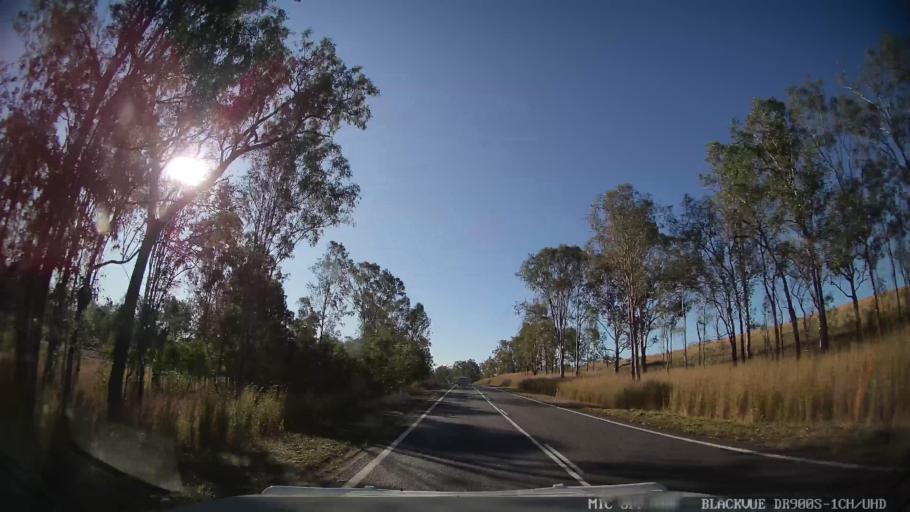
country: AU
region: Queensland
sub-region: Bundaberg
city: Sharon
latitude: -24.8322
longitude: 151.7091
